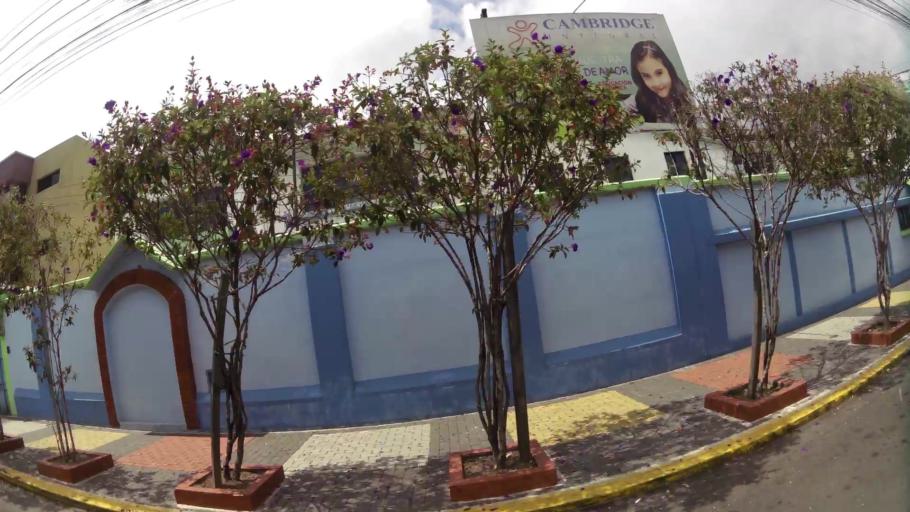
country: EC
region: Pichincha
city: Quito
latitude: -0.1907
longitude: -78.4945
